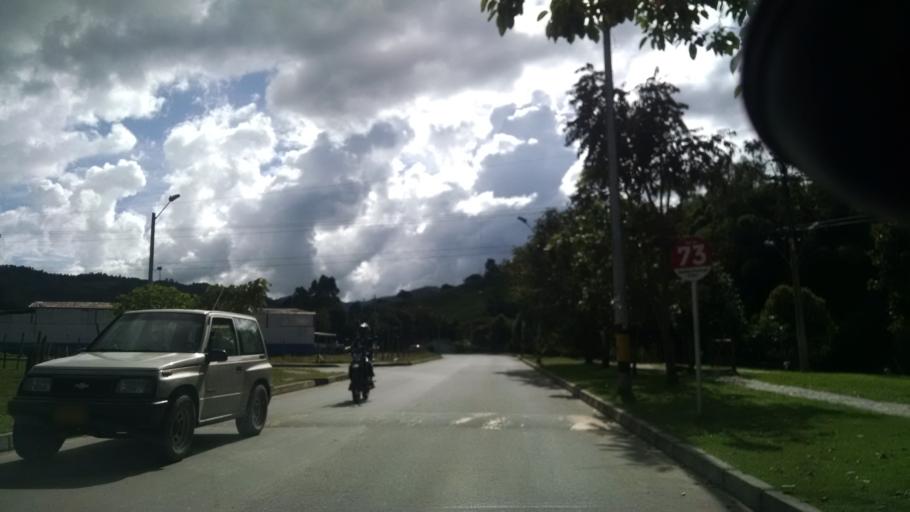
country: CO
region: Antioquia
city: El Retiro
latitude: 6.0618
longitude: -75.5034
